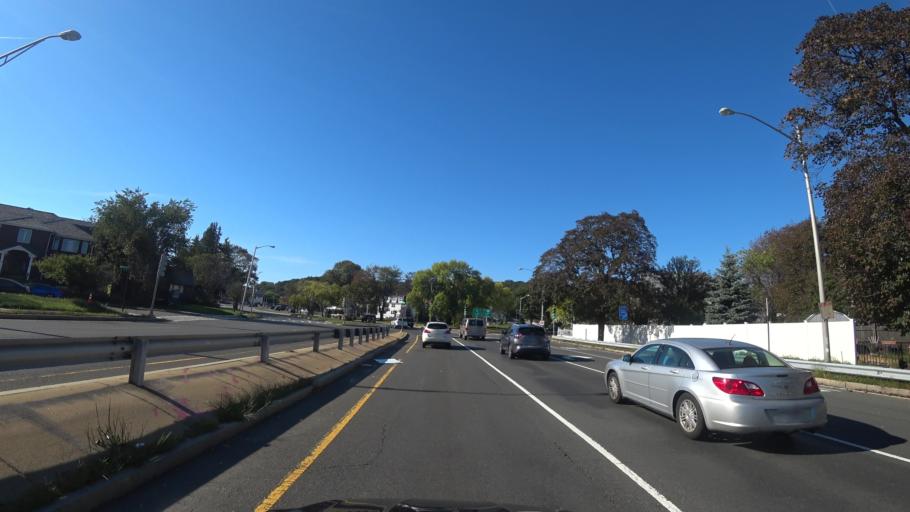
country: US
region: Massachusetts
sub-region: Middlesex County
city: Medford
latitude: 42.4225
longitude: -71.0864
